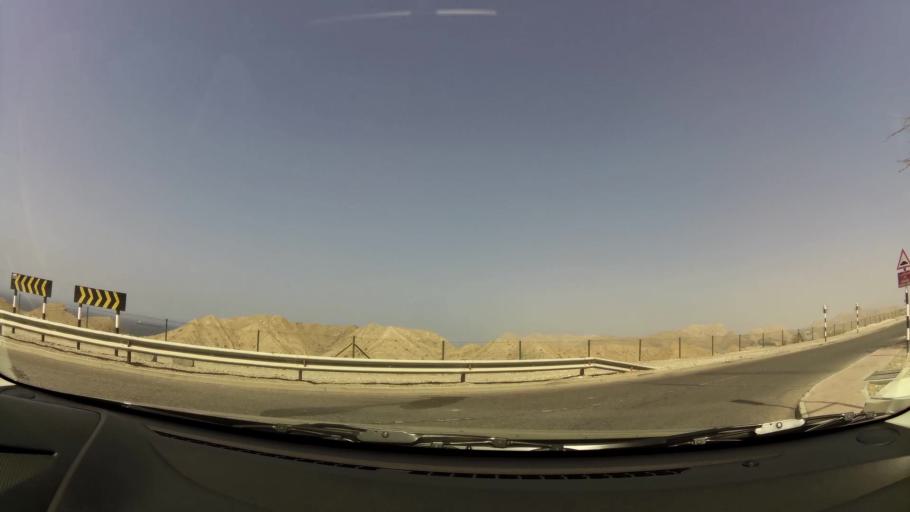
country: OM
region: Muhafazat Masqat
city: Muscat
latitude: 23.6307
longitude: 58.5001
